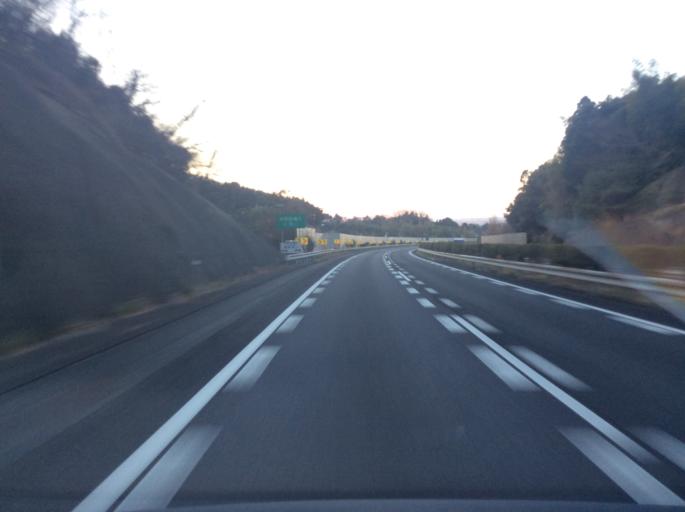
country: JP
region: Ibaraki
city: Funaishikawa
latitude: 36.5278
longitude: 140.5916
